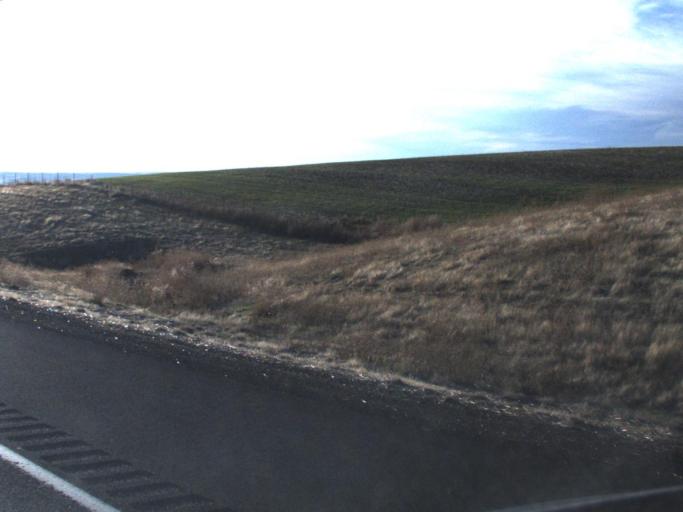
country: US
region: Washington
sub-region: Walla Walla County
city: Garrett
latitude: 46.0601
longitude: -118.4337
